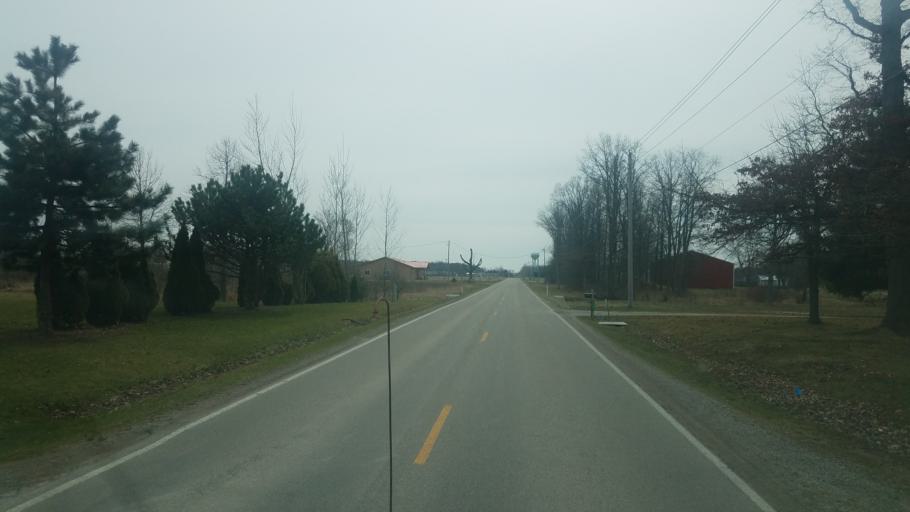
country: US
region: Ohio
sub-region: Huron County
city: Wakeman
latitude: 41.2245
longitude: -82.4914
